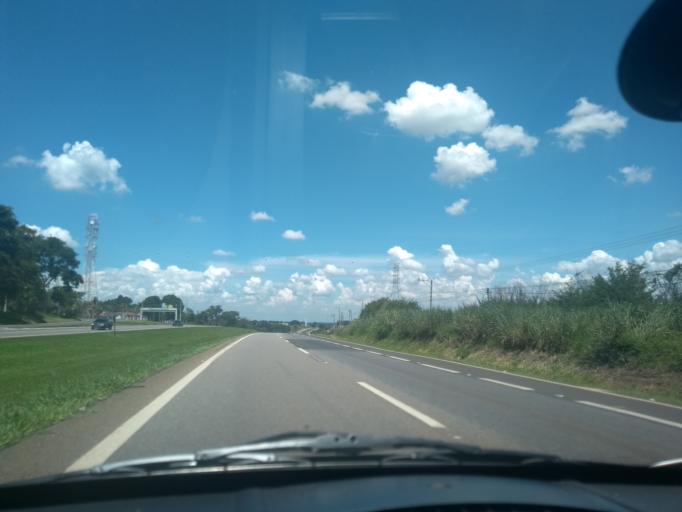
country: BR
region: Sao Paulo
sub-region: Mogi-Mirim
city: Mogi Mirim
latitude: -22.4899
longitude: -46.9815
